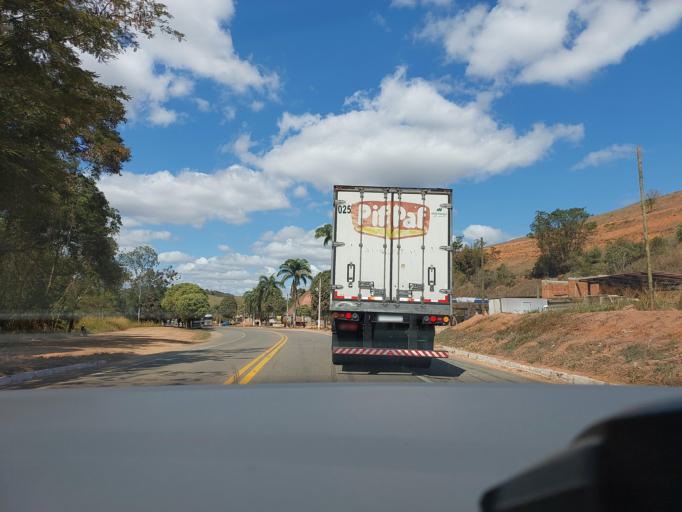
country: BR
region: Minas Gerais
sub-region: Muriae
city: Muriae
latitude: -21.1256
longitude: -42.2035
